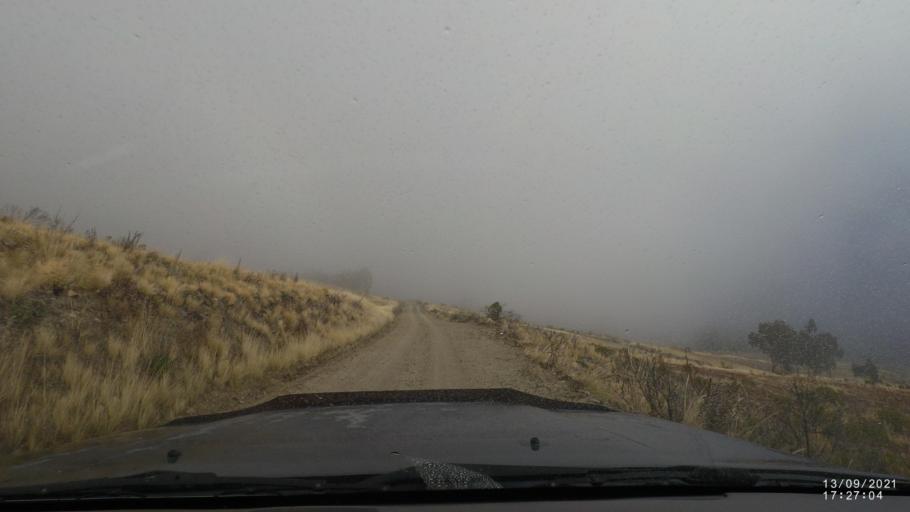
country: BO
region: Cochabamba
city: Colomi
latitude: -17.3611
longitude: -65.7850
